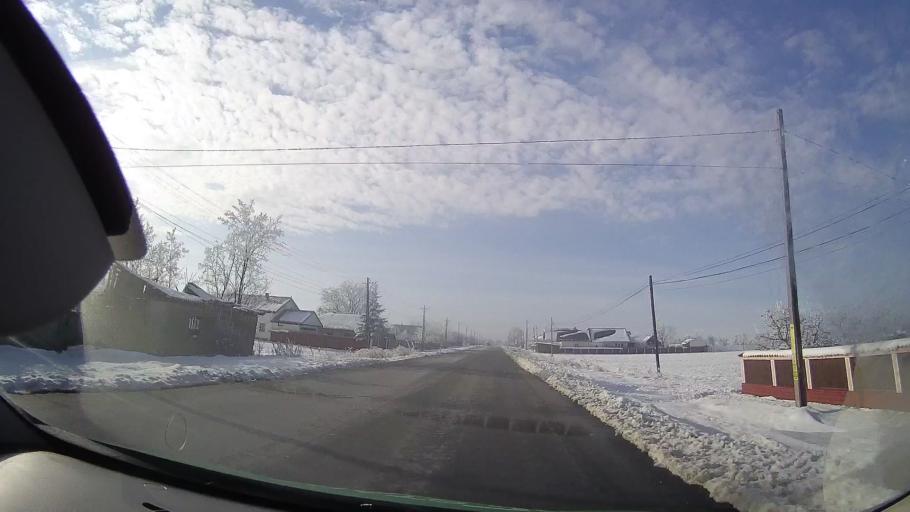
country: RO
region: Neamt
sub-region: Comuna Timisesti
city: Timisesti
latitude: 47.2338
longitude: 26.5282
